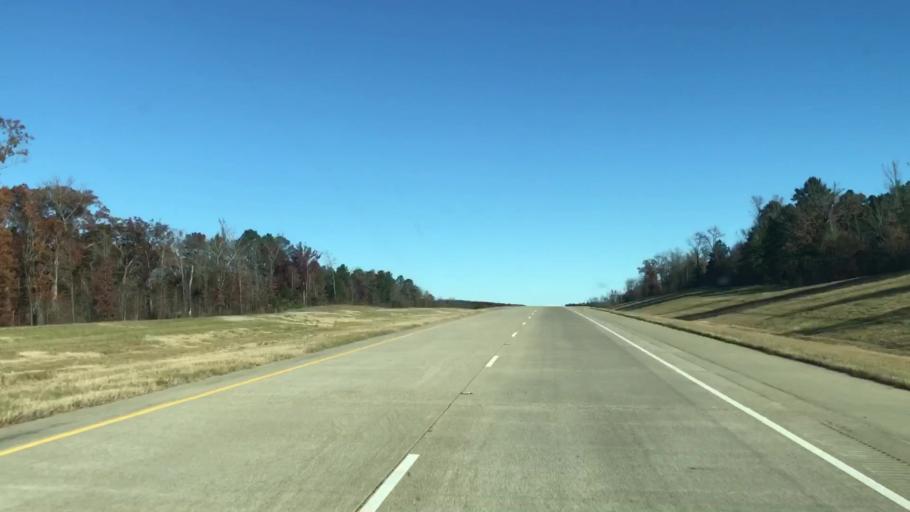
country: US
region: Louisiana
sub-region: Caddo Parish
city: Oil City
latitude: 32.7912
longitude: -93.8876
